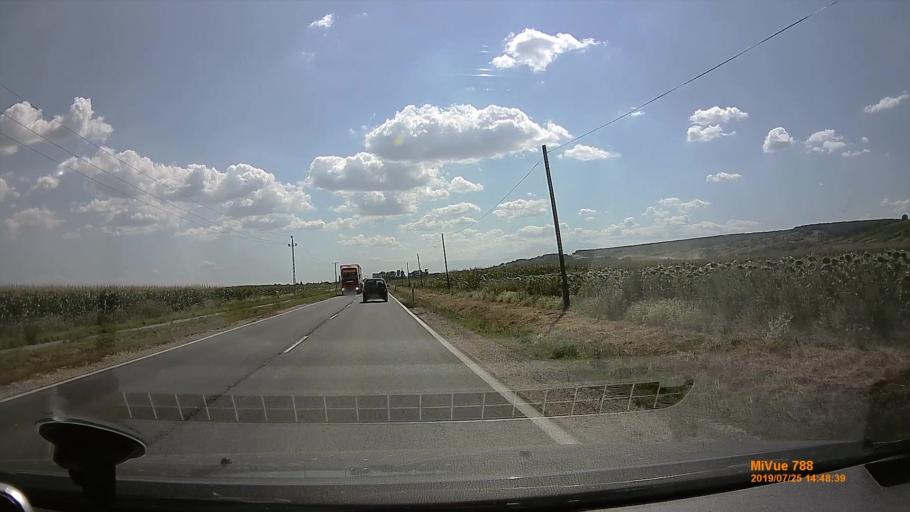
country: HU
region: Borsod-Abauj-Zemplen
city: Aszalo
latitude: 48.2354
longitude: 20.9640
